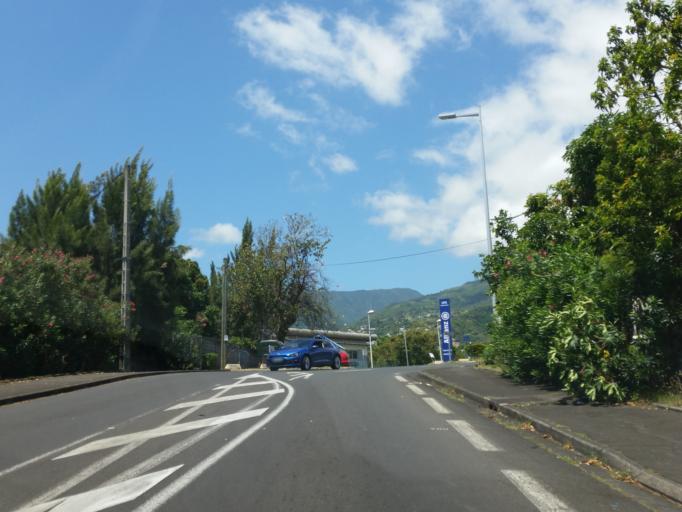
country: RE
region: Reunion
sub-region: Reunion
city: Saint-Denis
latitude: -20.9096
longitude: 55.4876
